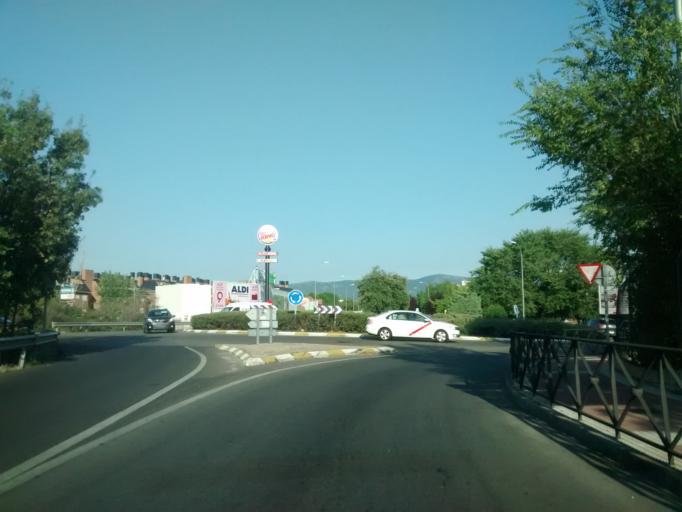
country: ES
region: Madrid
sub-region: Provincia de Madrid
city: Collado-Villalba
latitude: 40.6350
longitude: -4.0116
